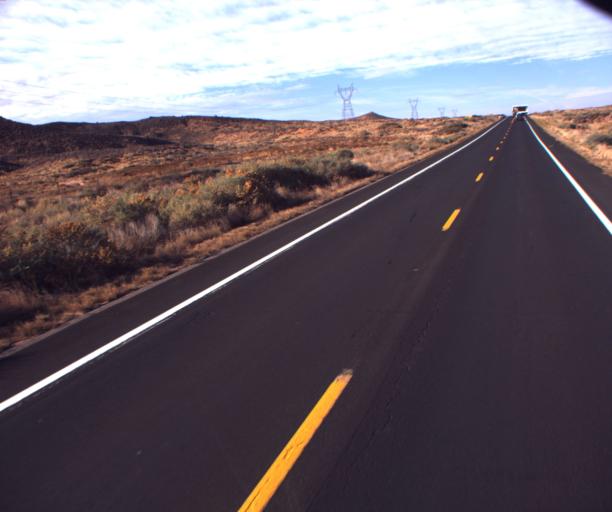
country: US
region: Arizona
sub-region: Apache County
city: Lukachukai
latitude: 36.9578
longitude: -109.4976
